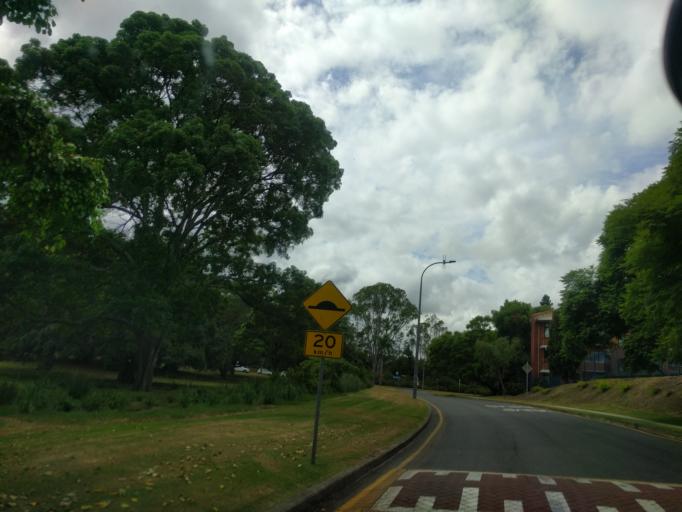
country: AU
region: Queensland
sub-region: Brisbane
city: Yeronga
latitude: -27.5005
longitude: 153.0179
